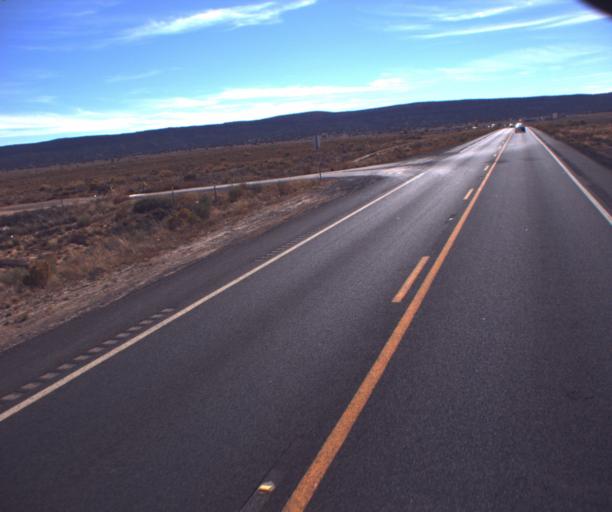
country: US
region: Arizona
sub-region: Coconino County
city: Kaibito
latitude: 36.4738
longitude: -110.6992
